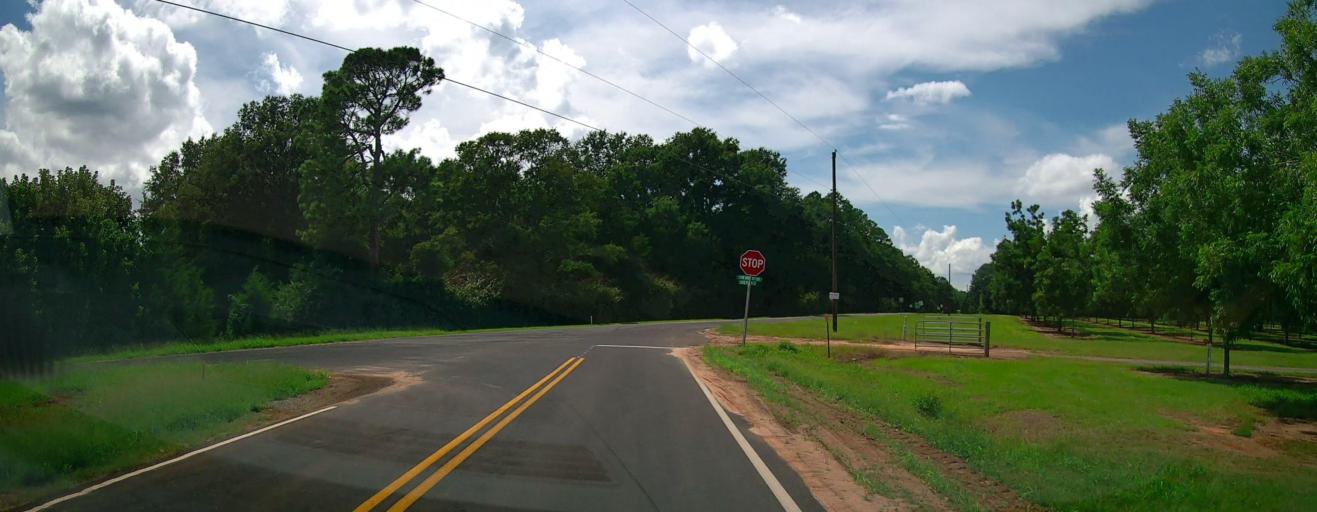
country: US
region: Georgia
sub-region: Macon County
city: Marshallville
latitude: 32.4564
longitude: -83.9228
